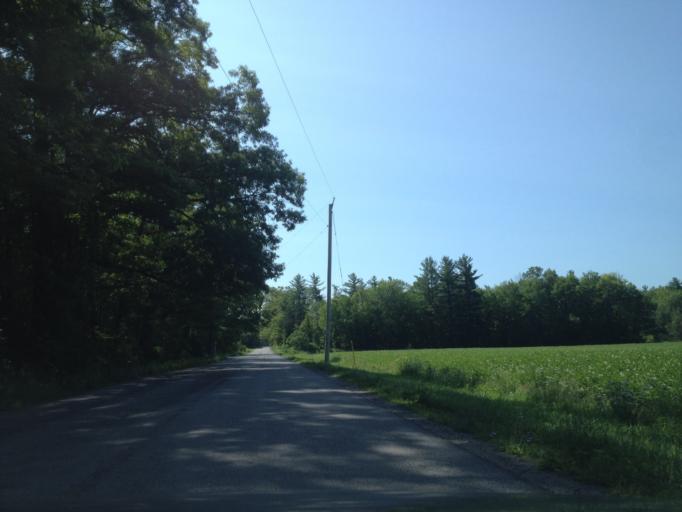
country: CA
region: Ontario
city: Norfolk County
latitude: 42.8200
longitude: -80.3808
